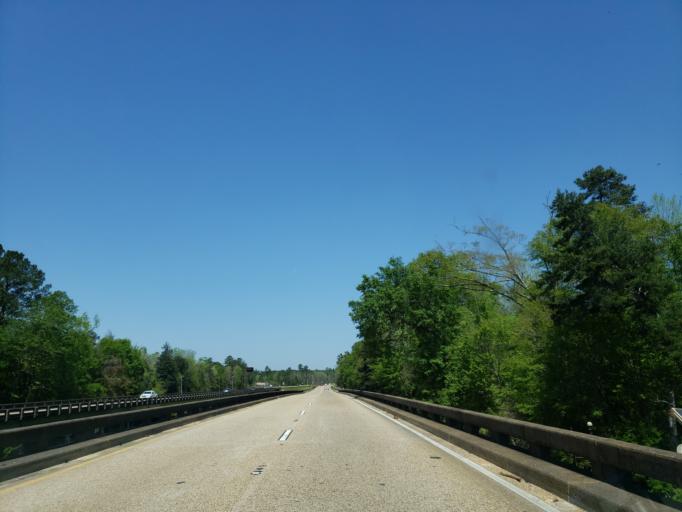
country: US
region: Mississippi
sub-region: Stone County
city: Wiggins
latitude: 31.0519
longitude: -89.2041
